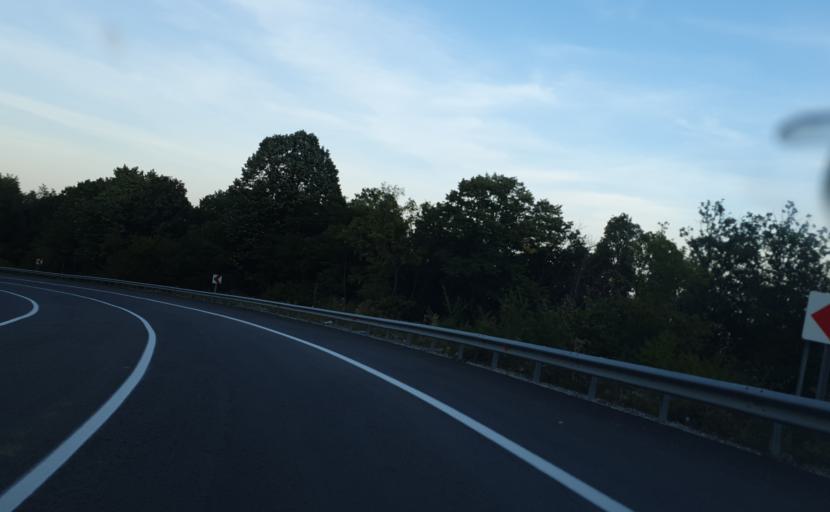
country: TR
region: Kirklareli
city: Sergen
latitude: 41.8118
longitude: 27.7458
